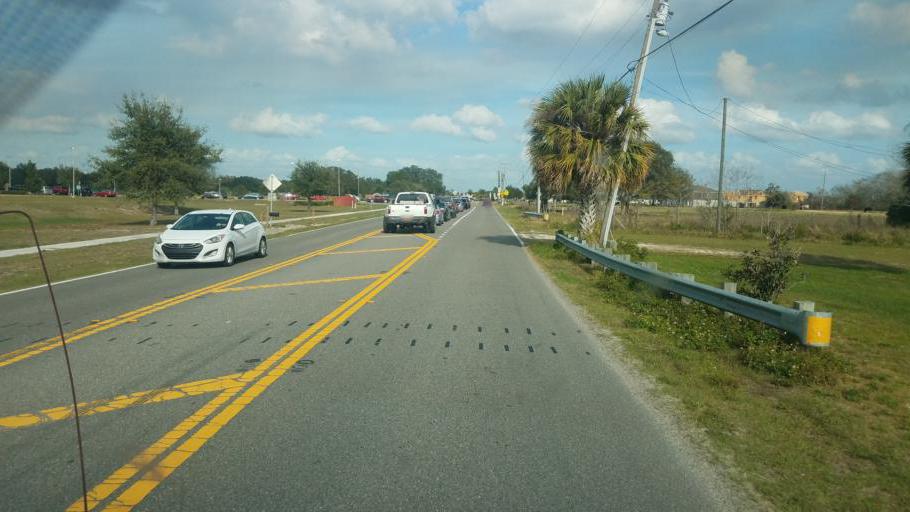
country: US
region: Florida
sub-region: Polk County
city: Loughman
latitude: 28.2266
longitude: -81.5845
